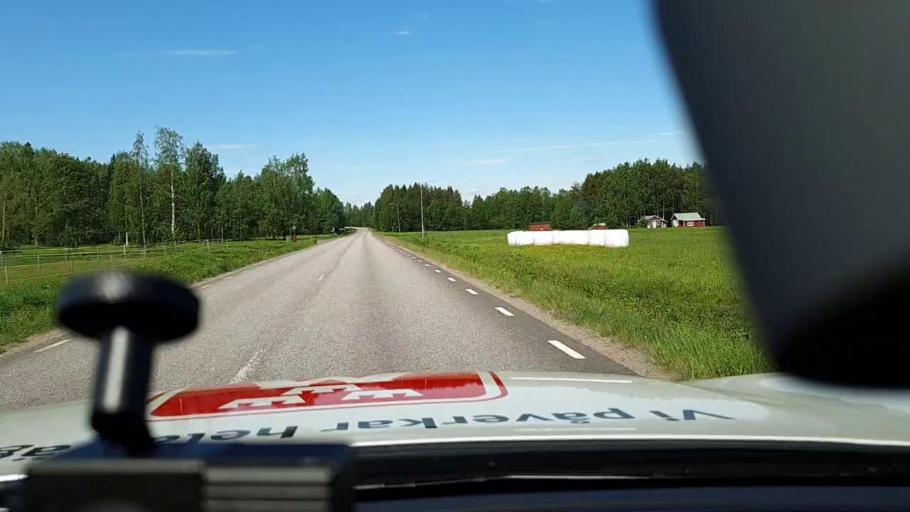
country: SE
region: Norrbotten
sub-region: Lulea Kommun
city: Sodra Sunderbyn
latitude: 65.6568
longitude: 21.8462
